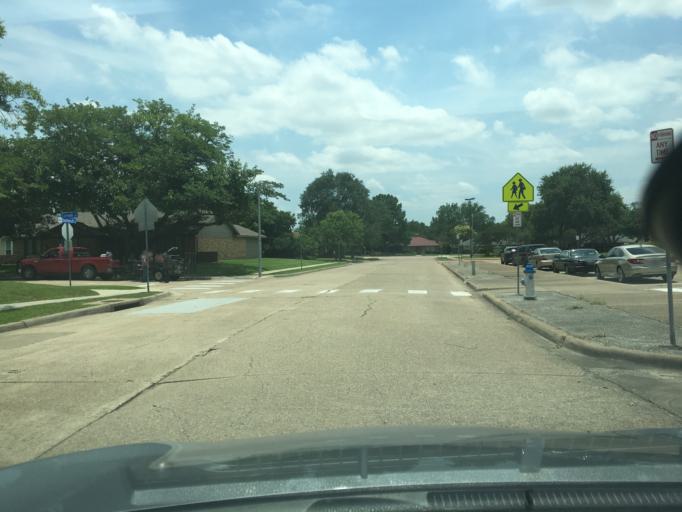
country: US
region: Texas
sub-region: Dallas County
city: Richardson
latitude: 32.9543
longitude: -96.6886
